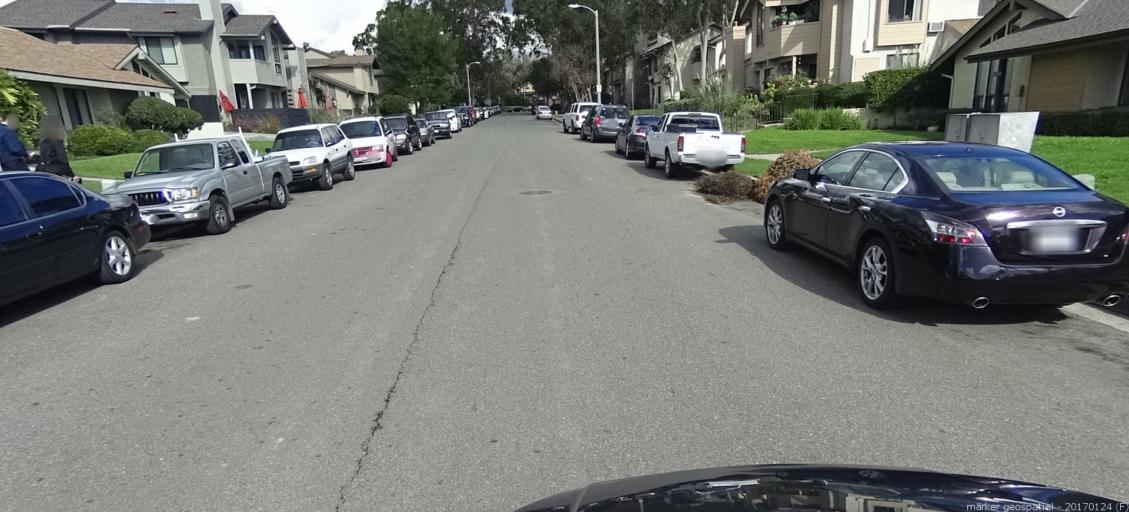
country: US
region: California
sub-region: Orange County
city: Laguna Hills
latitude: 33.6252
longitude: -117.6960
